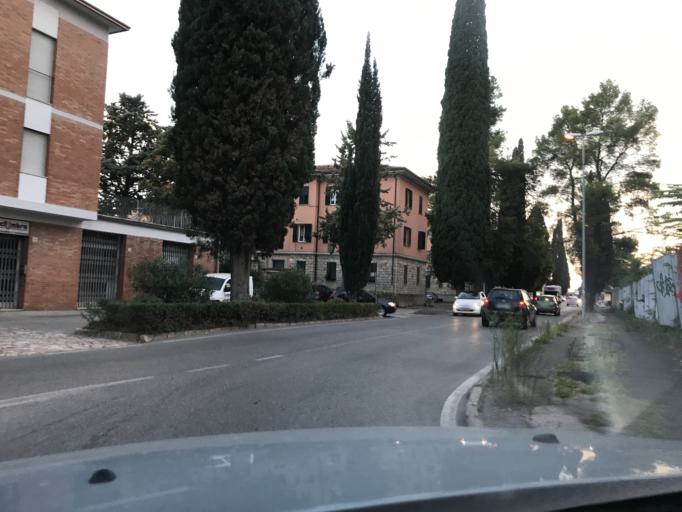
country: IT
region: Umbria
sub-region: Provincia di Perugia
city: Ponte Felcino
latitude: 43.0898
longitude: 12.4334
